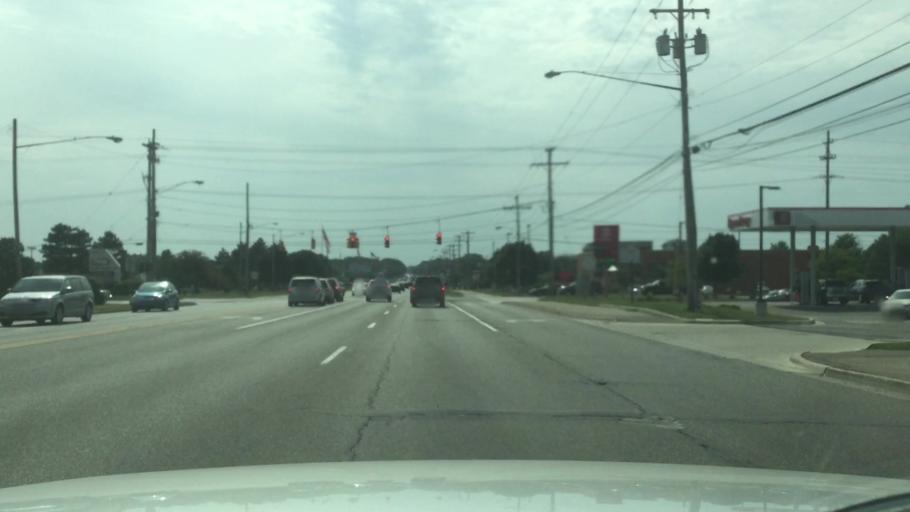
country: US
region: Michigan
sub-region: Genesee County
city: Swartz Creek
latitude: 43.0021
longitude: -83.7716
